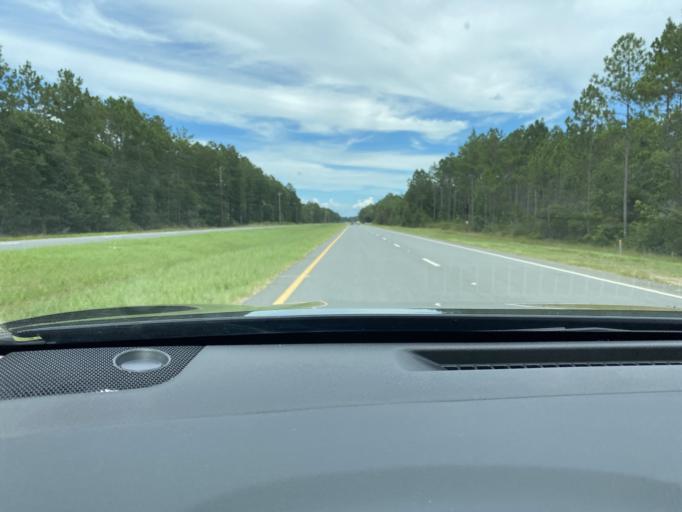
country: US
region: Georgia
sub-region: Brantley County
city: Nahunta
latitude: 31.1989
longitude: -82.0161
